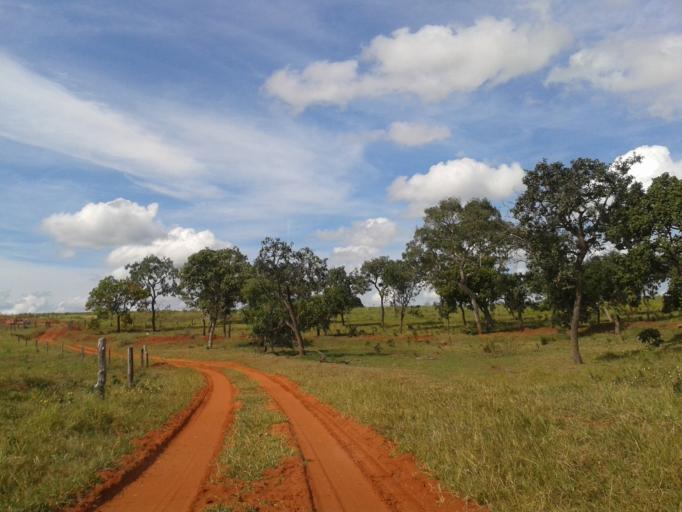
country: BR
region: Minas Gerais
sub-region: Campina Verde
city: Campina Verde
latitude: -19.4547
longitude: -49.6829
